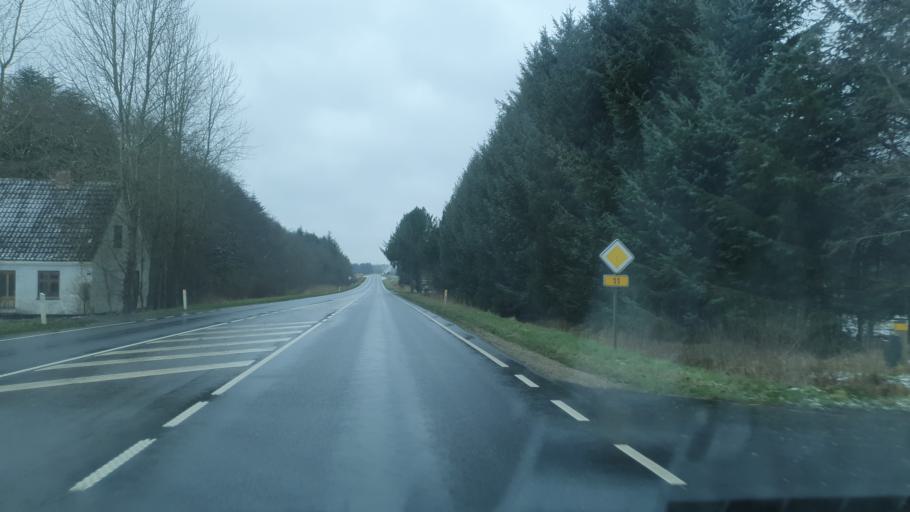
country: DK
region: North Denmark
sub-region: Jammerbugt Kommune
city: Fjerritslev
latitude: 57.0881
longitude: 9.3401
